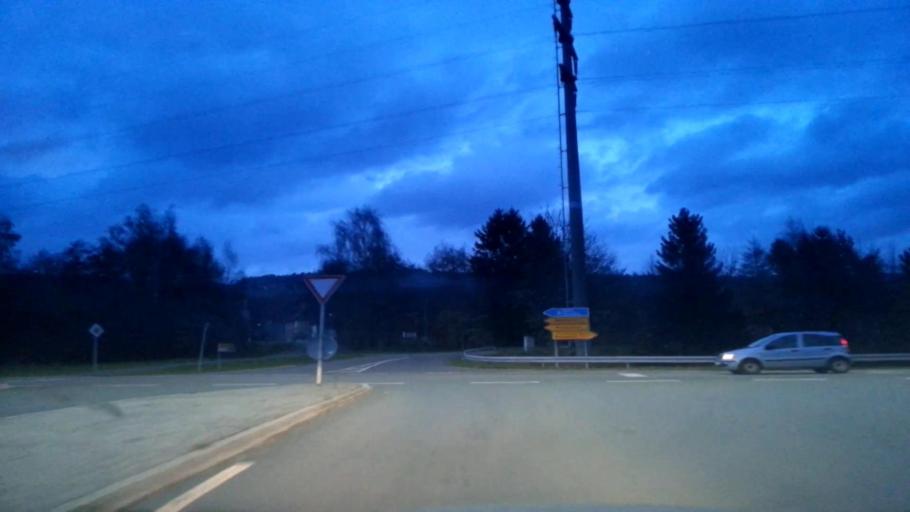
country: DE
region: Bavaria
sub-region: Upper Franconia
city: Kirchenpingarten
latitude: 49.9409
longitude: 11.7403
